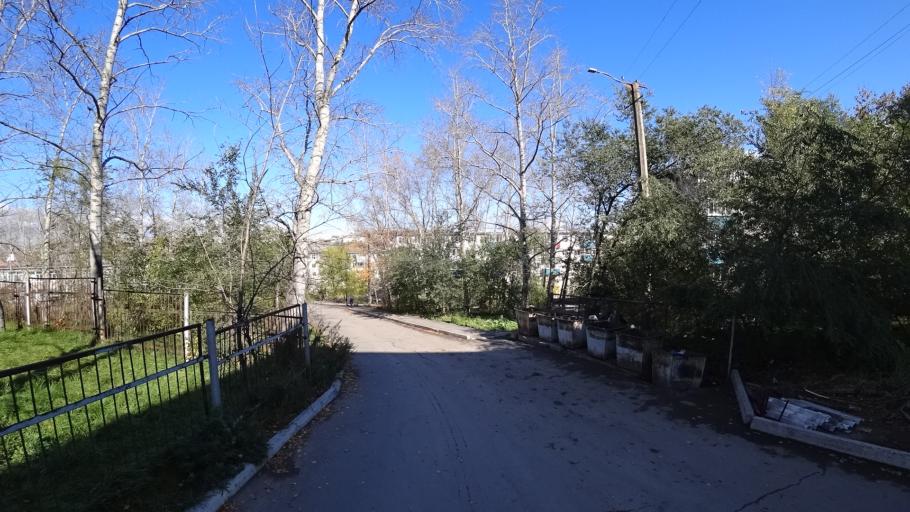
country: RU
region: Khabarovsk Krai
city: Amursk
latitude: 50.2209
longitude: 136.9088
